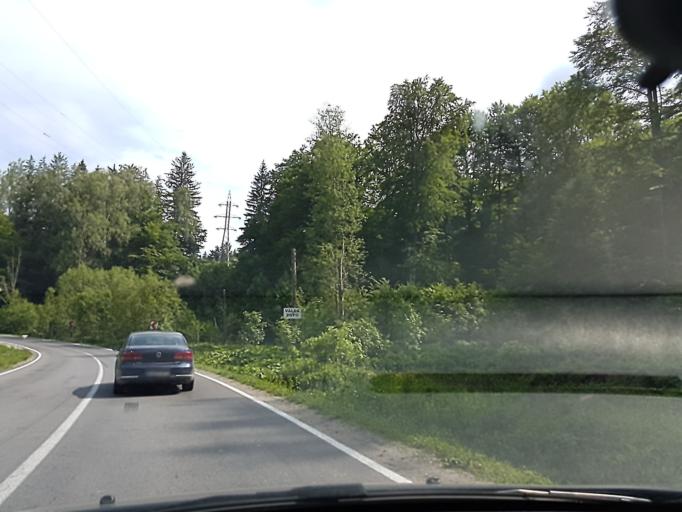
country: RO
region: Prahova
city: Maneciu
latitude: 45.3584
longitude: 25.9411
